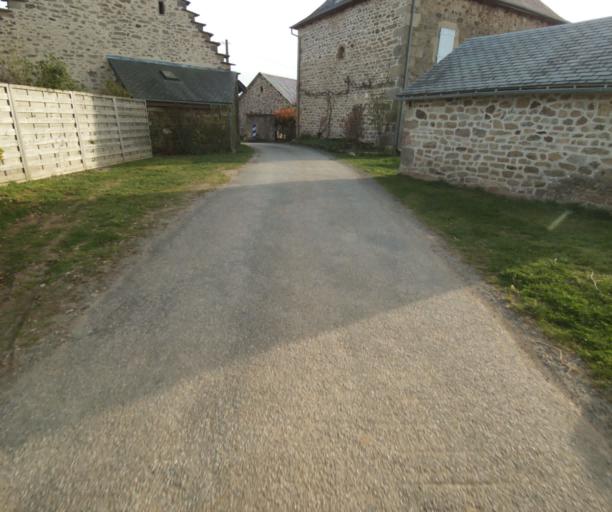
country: FR
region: Limousin
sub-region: Departement de la Correze
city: Correze
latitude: 45.3655
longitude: 1.8321
